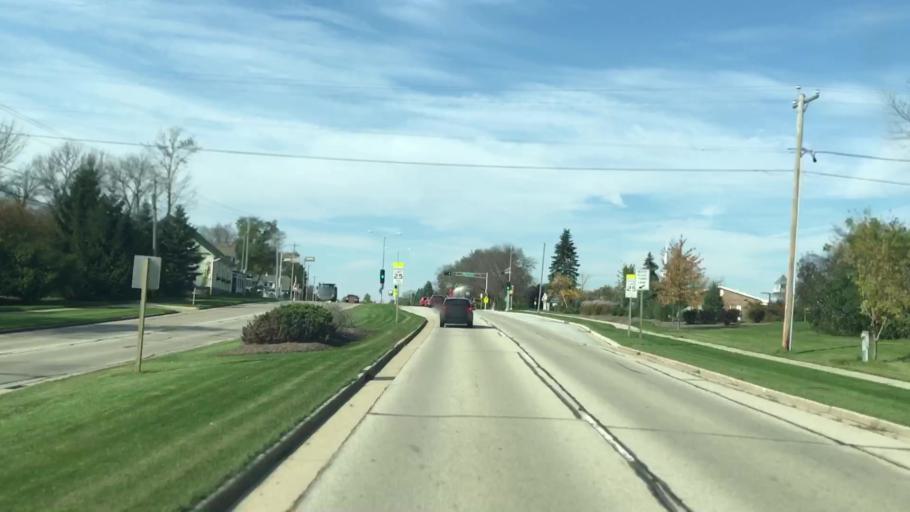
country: US
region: Wisconsin
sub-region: Ozaukee County
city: Thiensville
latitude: 43.2216
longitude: -87.9423
